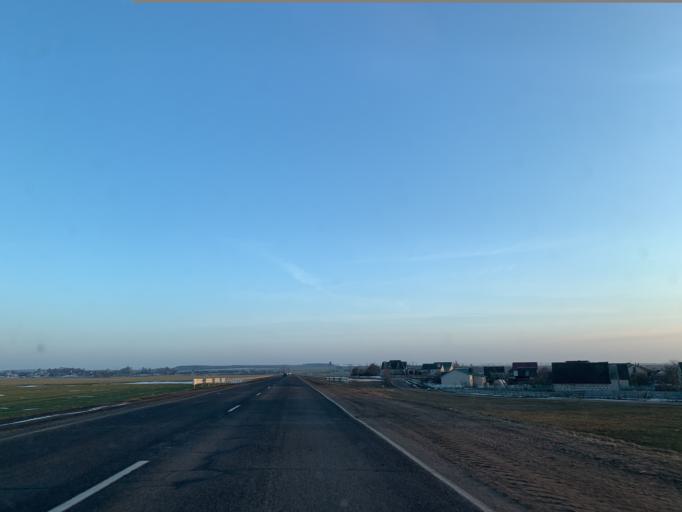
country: BY
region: Minsk
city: Haradzyeya
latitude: 53.3131
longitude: 26.5649
